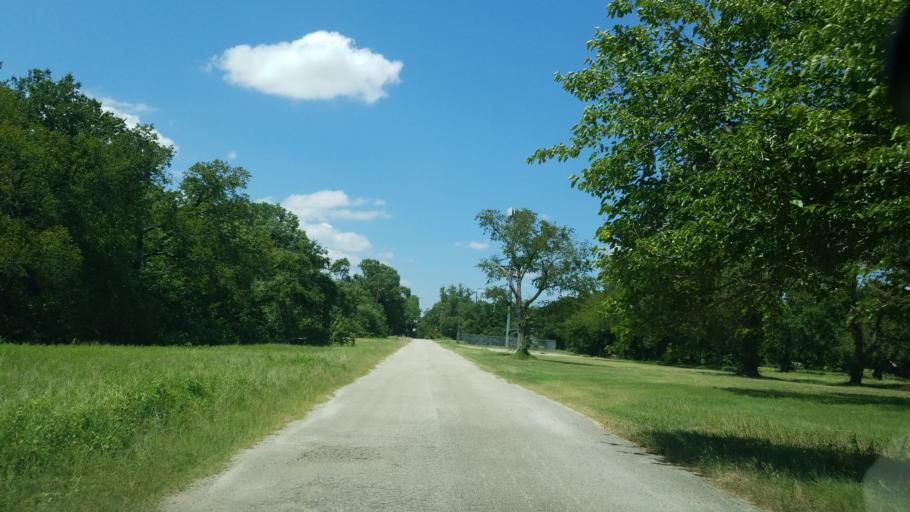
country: US
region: Texas
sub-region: Dallas County
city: Dallas
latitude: 32.7473
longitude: -96.7260
